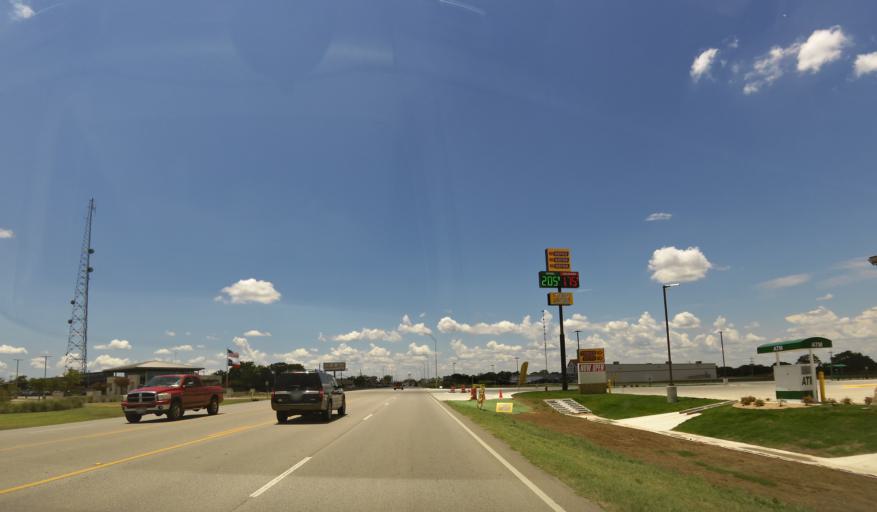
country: US
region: Texas
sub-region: Lee County
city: Giddings
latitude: 30.1781
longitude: -96.9065
